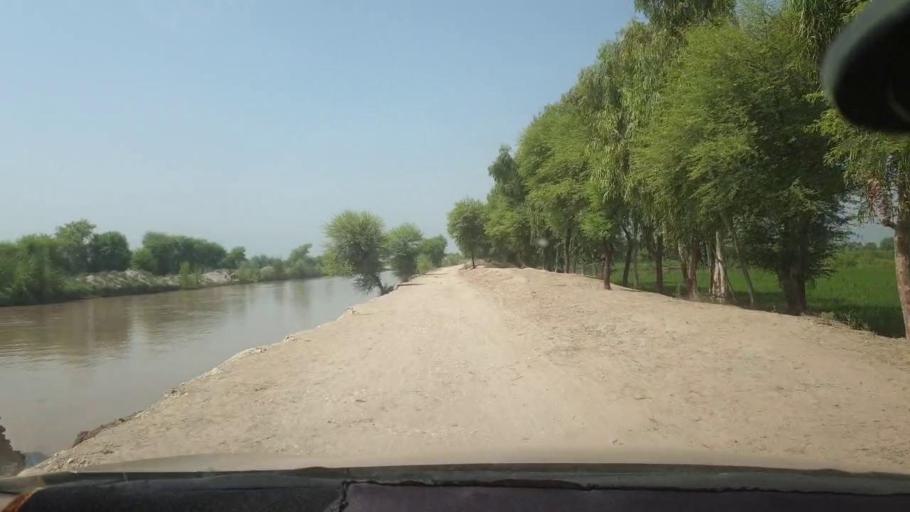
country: PK
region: Sindh
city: Shahdadkot
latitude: 27.7130
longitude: 67.9339
